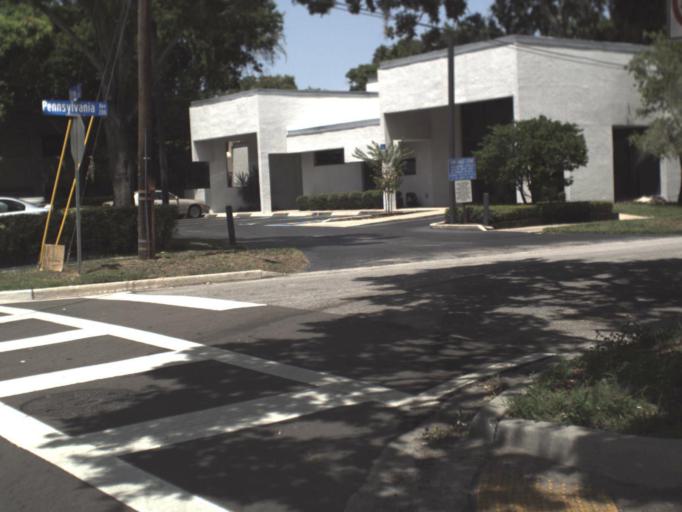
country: US
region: Florida
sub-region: Pinellas County
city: Clearwater
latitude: 27.9682
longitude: -82.7931
